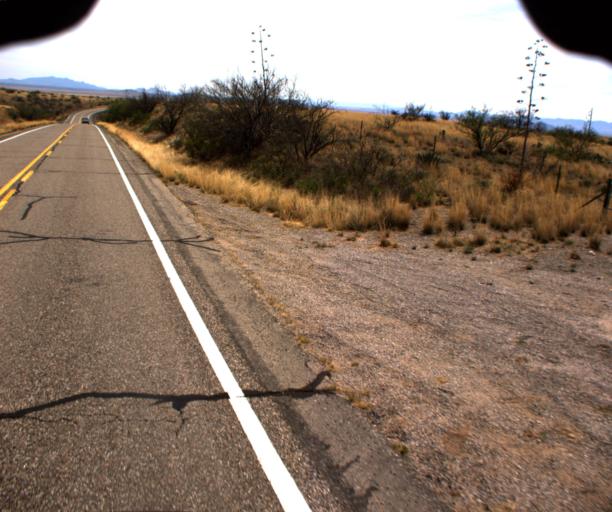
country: US
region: Arizona
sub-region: Cochise County
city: Willcox
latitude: 32.1482
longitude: -109.5650
